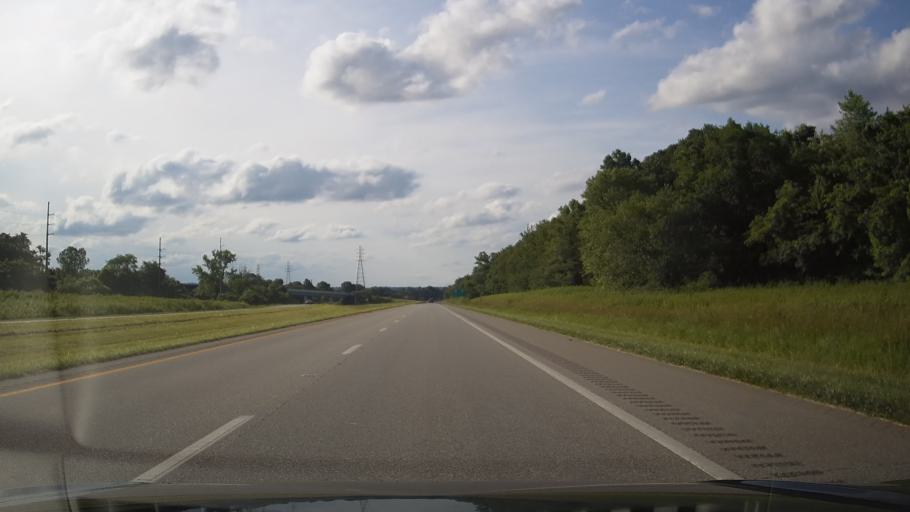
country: US
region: Ohio
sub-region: Scioto County
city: Franklin Furnace
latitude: 38.6350
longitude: -82.8448
